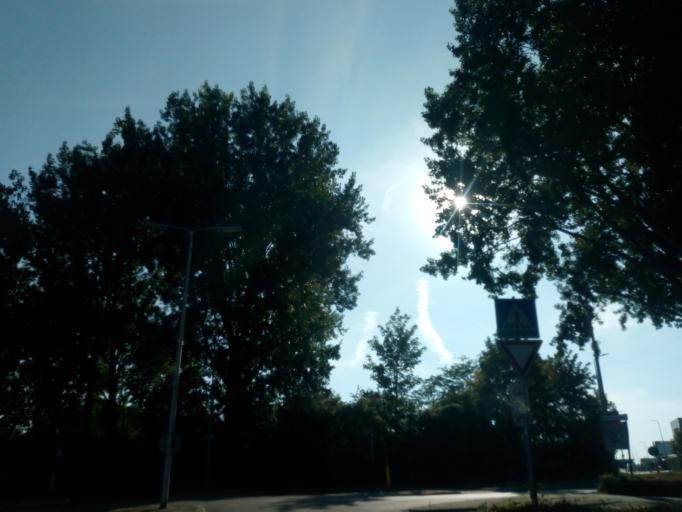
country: NL
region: South Holland
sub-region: Gemeente Alphen aan den Rijn
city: Alphen aan den Rijn
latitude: 52.1472
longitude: 4.6510
